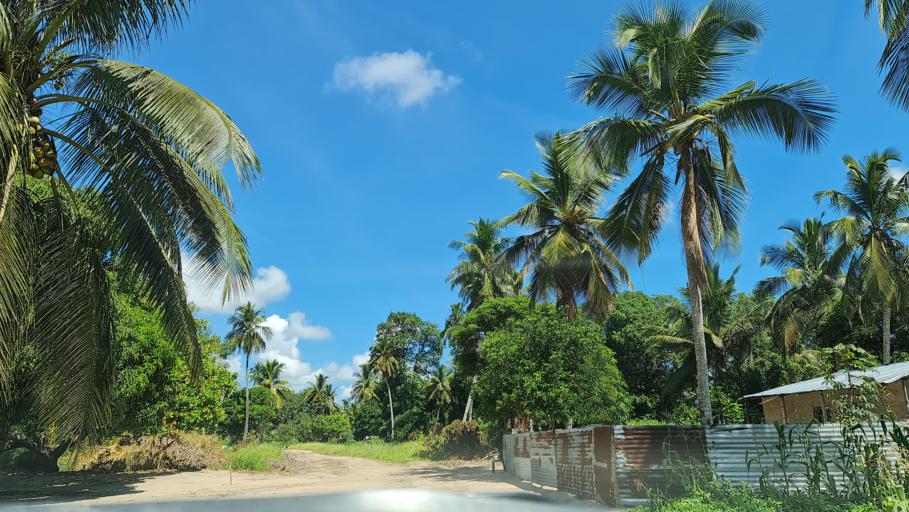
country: MZ
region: Zambezia
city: Quelimane
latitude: -17.3837
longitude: 37.5229
